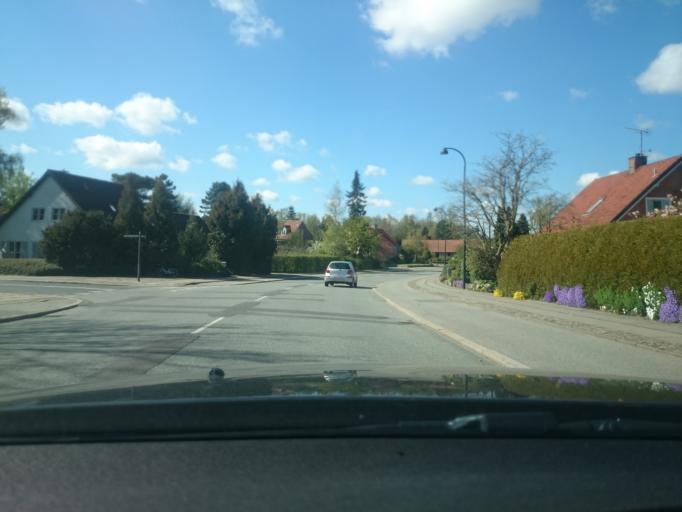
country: DK
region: Capital Region
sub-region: Lyngby-Tarbaek Kommune
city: Kongens Lyngby
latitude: 55.7605
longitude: 12.5426
